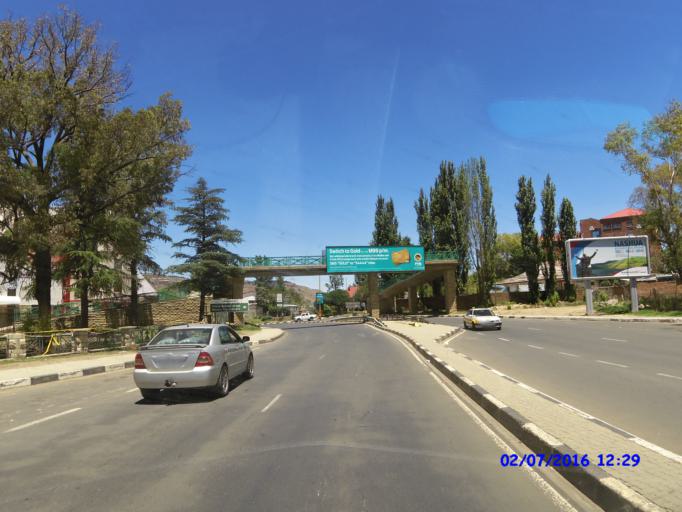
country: LS
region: Maseru
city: Maseru
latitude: -29.3130
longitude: 27.4774
